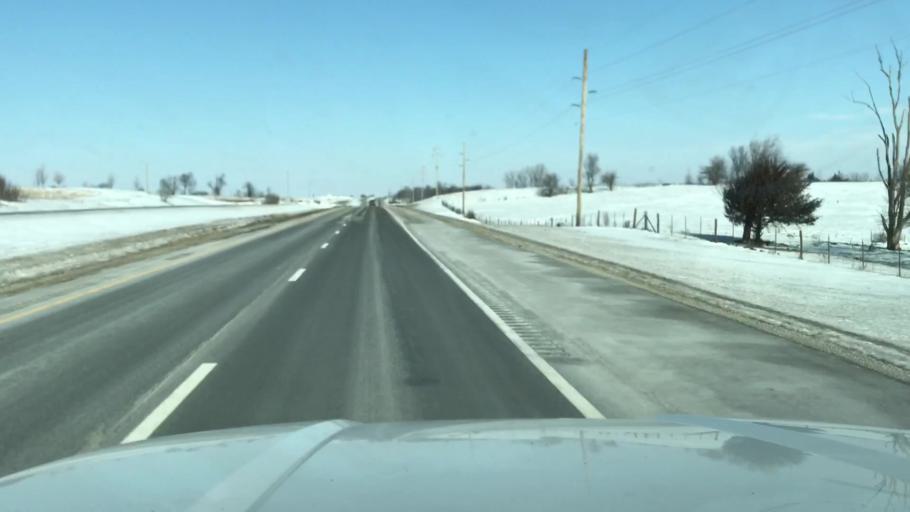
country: US
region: Missouri
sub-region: Nodaway County
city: Maryville
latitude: 40.2089
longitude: -94.8677
